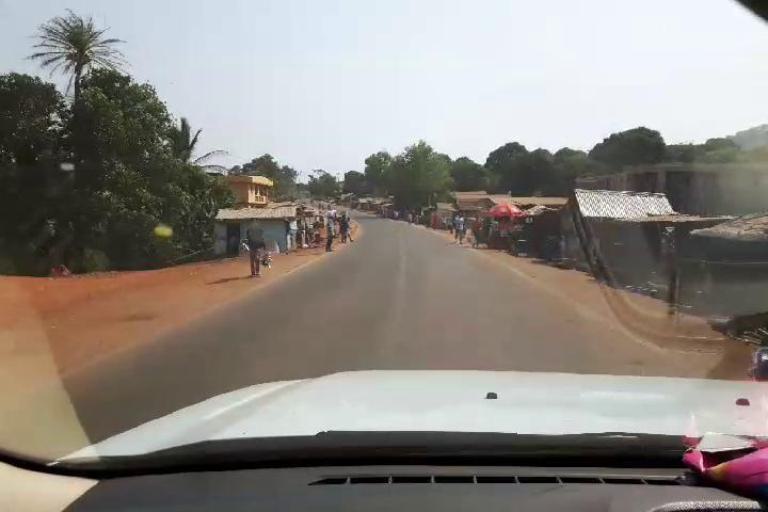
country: SL
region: Western Area
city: Waterloo
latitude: 8.2091
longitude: -13.1049
